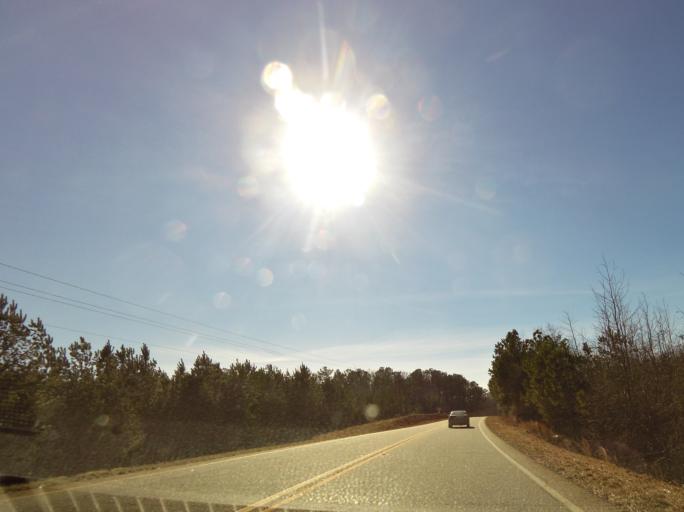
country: US
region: Georgia
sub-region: Crawford County
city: Roberta
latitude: 32.8756
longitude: -84.0311
